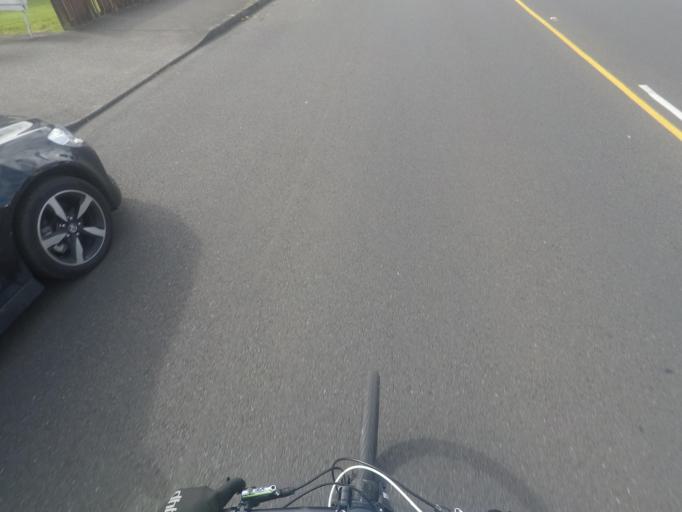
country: NZ
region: Auckland
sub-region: Auckland
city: Auckland
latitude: -36.9137
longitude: 174.7771
